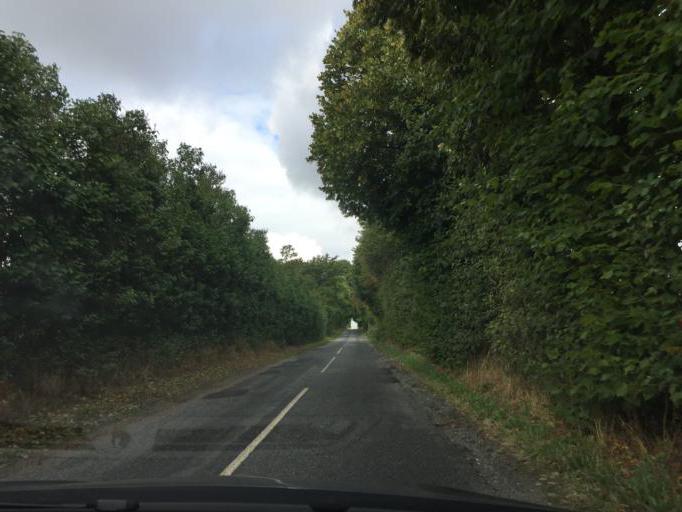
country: DK
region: South Denmark
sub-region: Assens Kommune
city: Harby
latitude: 55.1947
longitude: 10.1973
